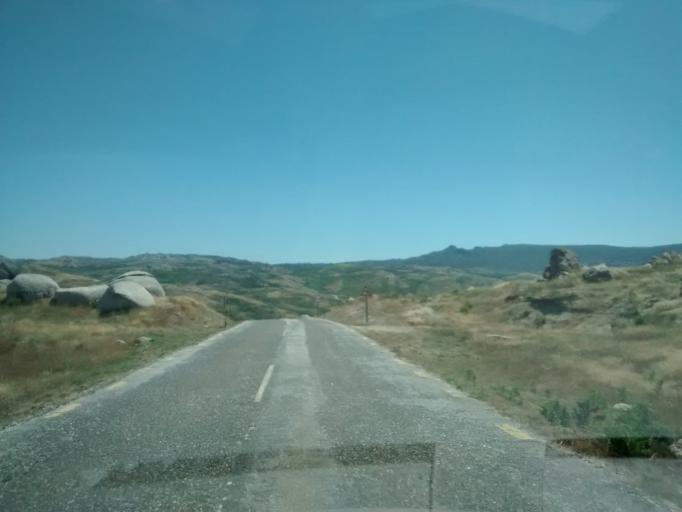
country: PT
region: Guarda
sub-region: Seia
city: Seia
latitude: 40.4202
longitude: -7.6302
